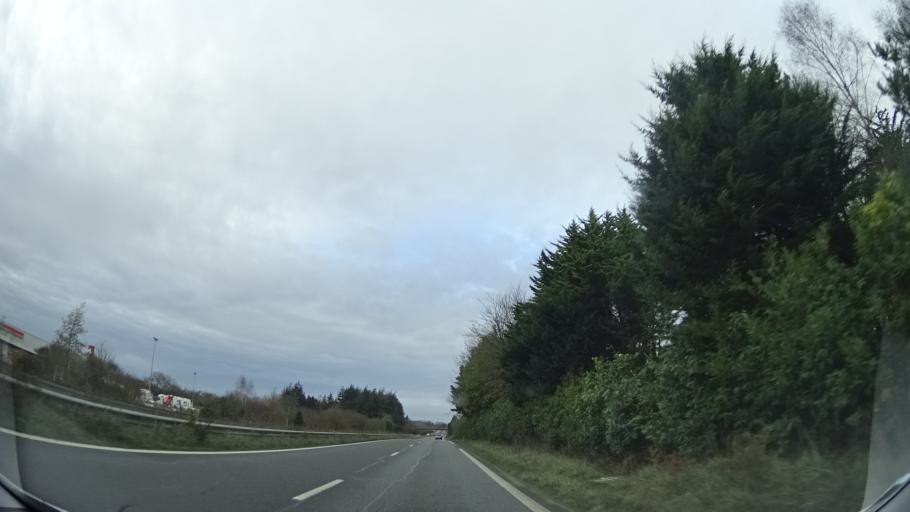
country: FR
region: Brittany
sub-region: Departement des Cotes-d'Armor
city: Trelivan
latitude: 48.4440
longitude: -2.1158
